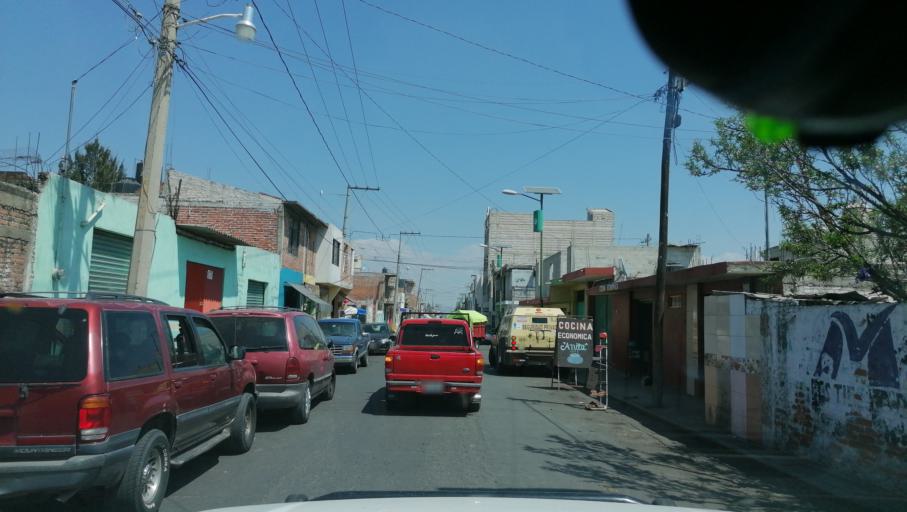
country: MX
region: Puebla
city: Huejotzingo
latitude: 19.1586
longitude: -98.4124
